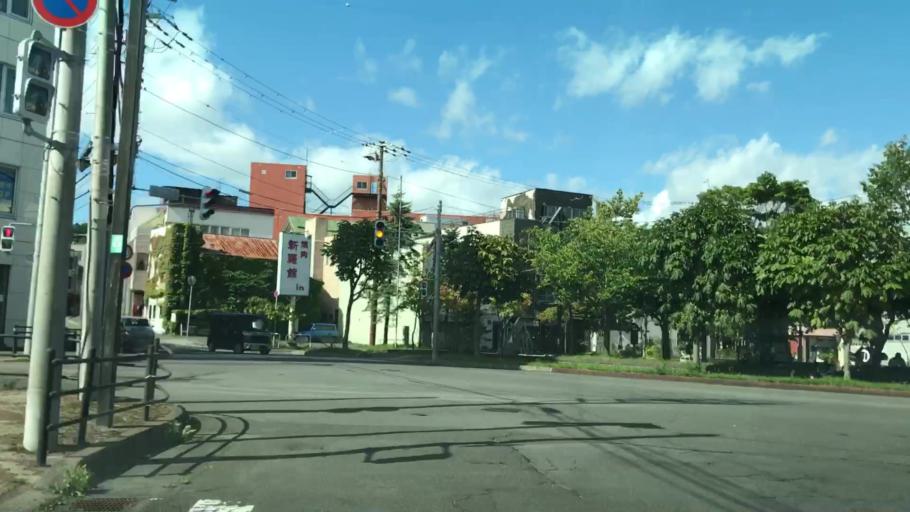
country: JP
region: Hokkaido
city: Muroran
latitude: 42.3162
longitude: 140.9719
